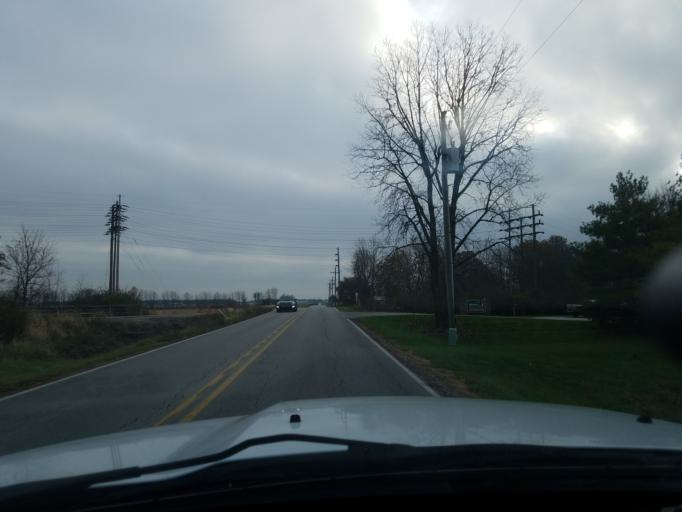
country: US
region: Indiana
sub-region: Delaware County
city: Muncie
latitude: 40.2335
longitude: -85.4041
